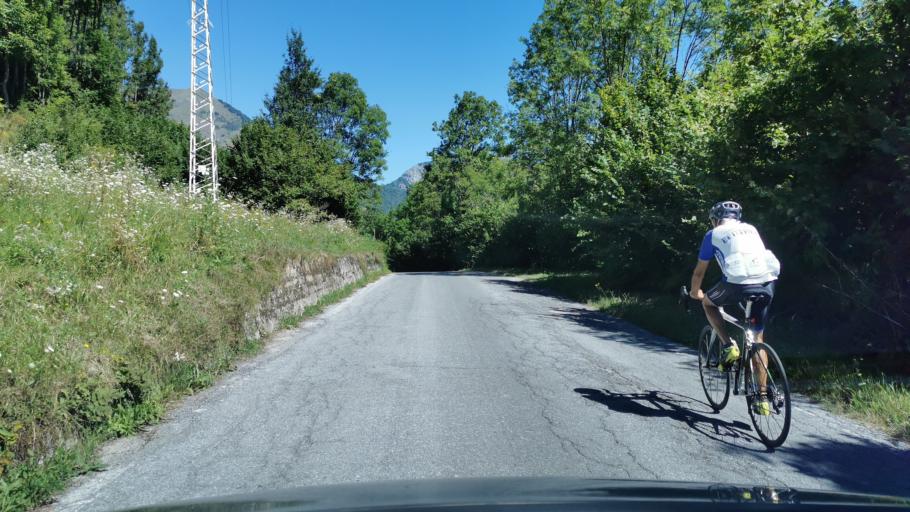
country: IT
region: Piedmont
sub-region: Provincia di Cuneo
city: Entracque
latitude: 44.2412
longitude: 7.3901
